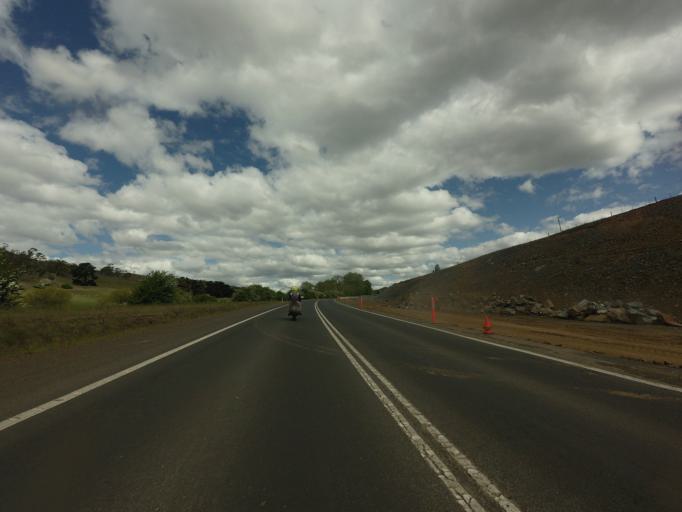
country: AU
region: Tasmania
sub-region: Brighton
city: Bridgewater
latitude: -42.2496
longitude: 147.4071
